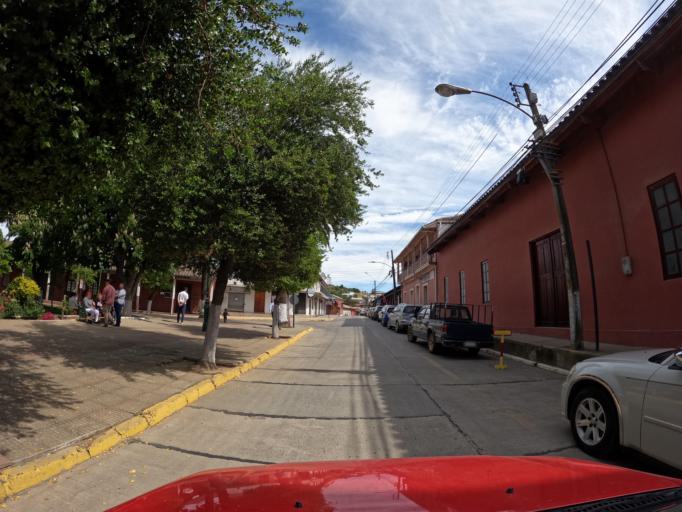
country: CL
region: Maule
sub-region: Provincia de Talca
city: Constitucion
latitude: -35.0938
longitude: -72.0184
